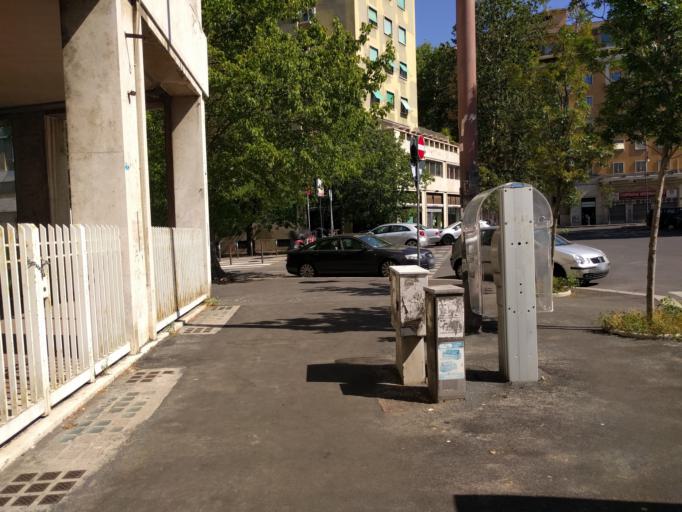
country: VA
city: Vatican City
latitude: 41.9272
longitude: 12.4617
